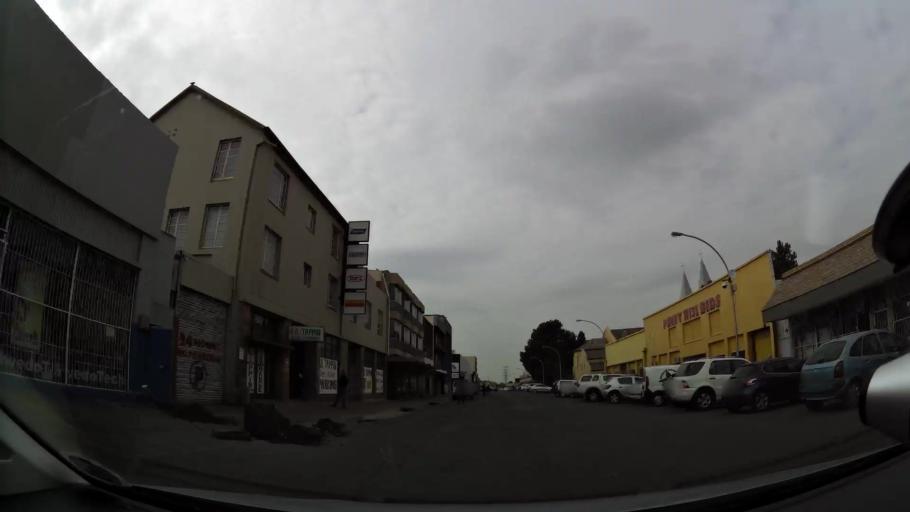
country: ZA
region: Orange Free State
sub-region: Mangaung Metropolitan Municipality
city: Bloemfontein
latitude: -29.1153
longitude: 26.2212
